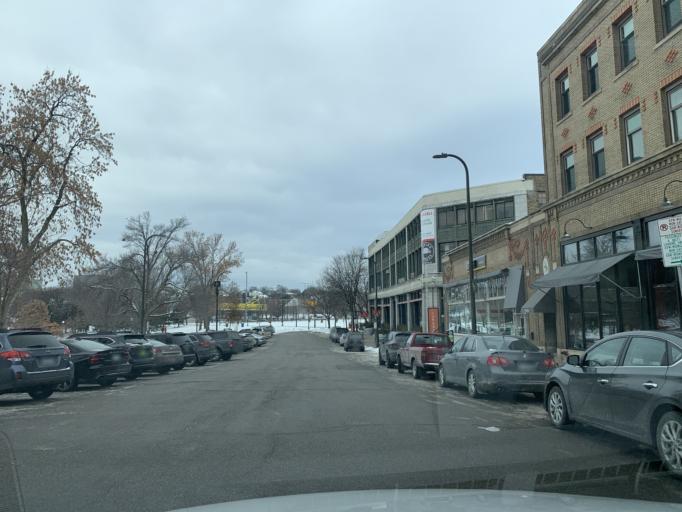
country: US
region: Minnesota
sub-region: Hennepin County
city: Minneapolis
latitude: 44.9715
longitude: -93.2853
